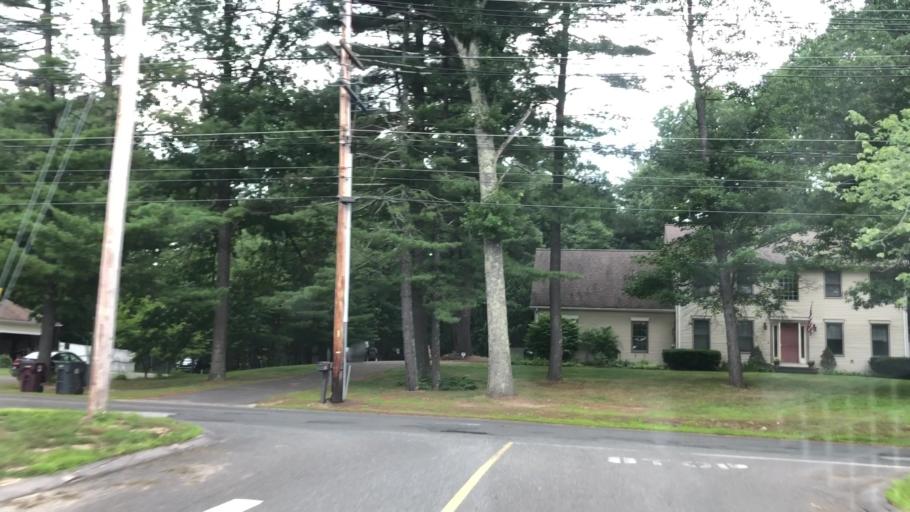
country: US
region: Massachusetts
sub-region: Hampden County
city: Westfield
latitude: 42.1723
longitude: -72.7482
